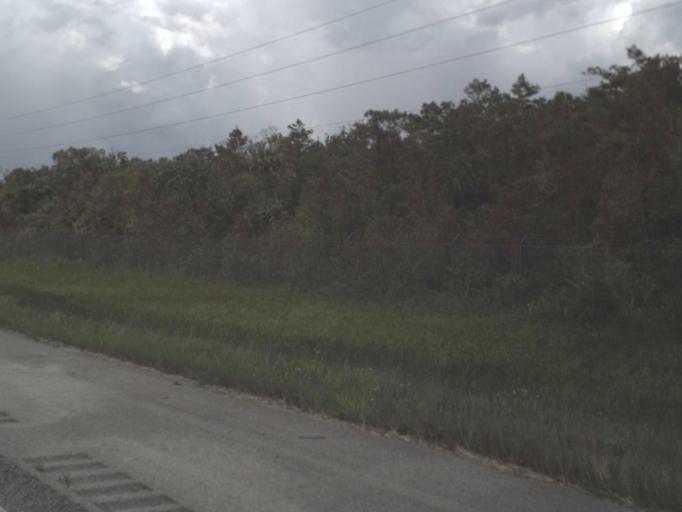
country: US
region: Florida
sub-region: Collier County
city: Immokalee
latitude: 26.1594
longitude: -81.2526
